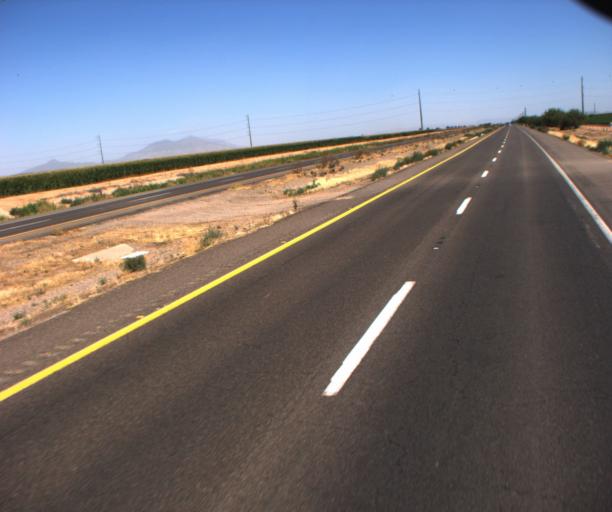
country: US
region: Arizona
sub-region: Pinal County
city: Maricopa
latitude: 32.9563
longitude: -112.0477
